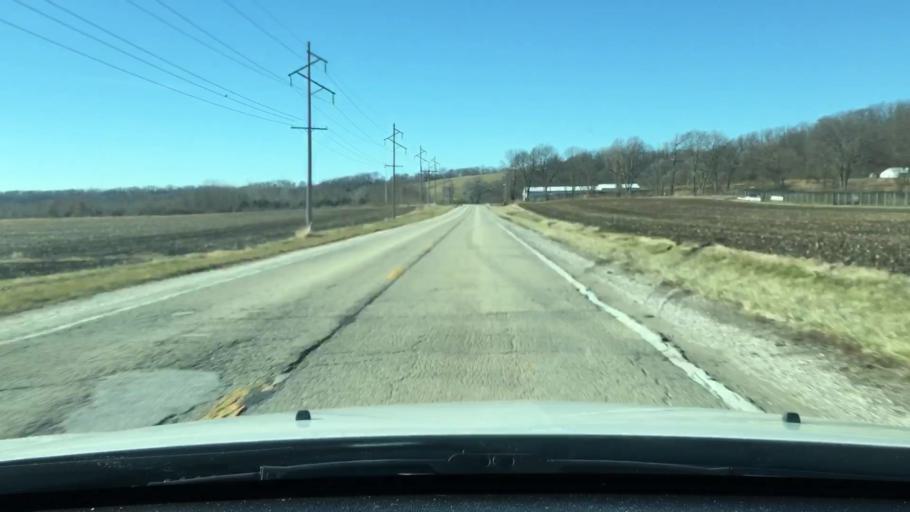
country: US
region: Illinois
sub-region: Fulton County
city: Astoria
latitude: 40.1754
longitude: -90.2740
